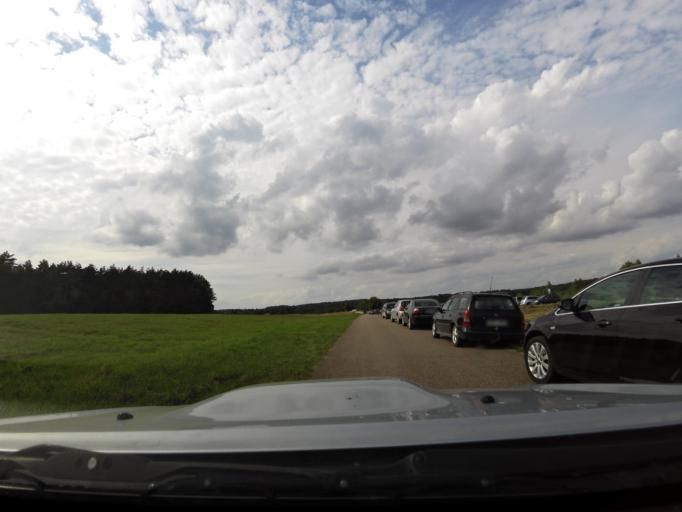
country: LT
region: Vilnius County
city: Elektrenai
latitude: 54.8371
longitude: 24.5676
